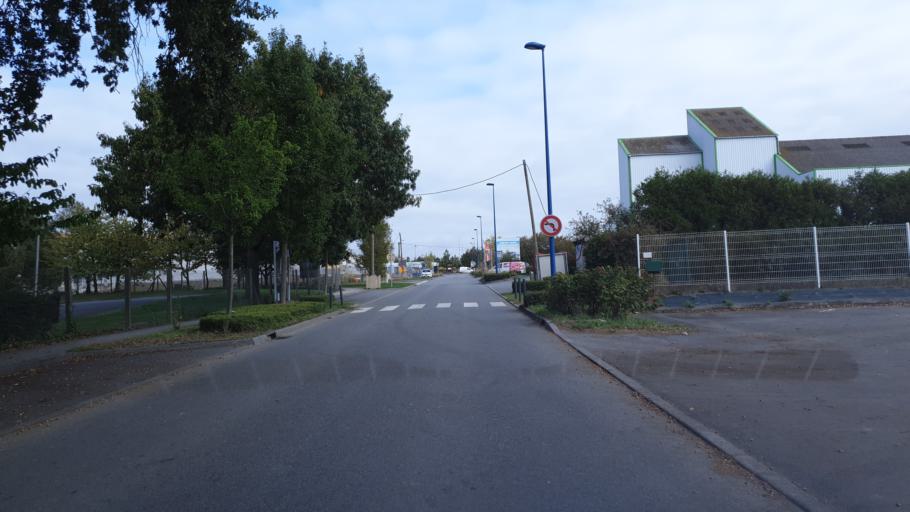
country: FR
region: Brittany
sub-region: Departement d'Ille-et-Vilaine
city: Janze
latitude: 47.9555
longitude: -1.4904
